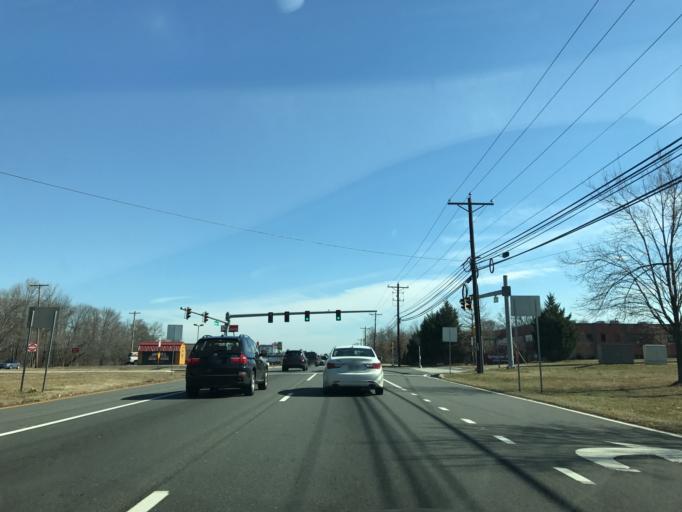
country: US
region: Delaware
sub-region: New Castle County
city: Glasgow
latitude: 39.6036
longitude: -75.7561
